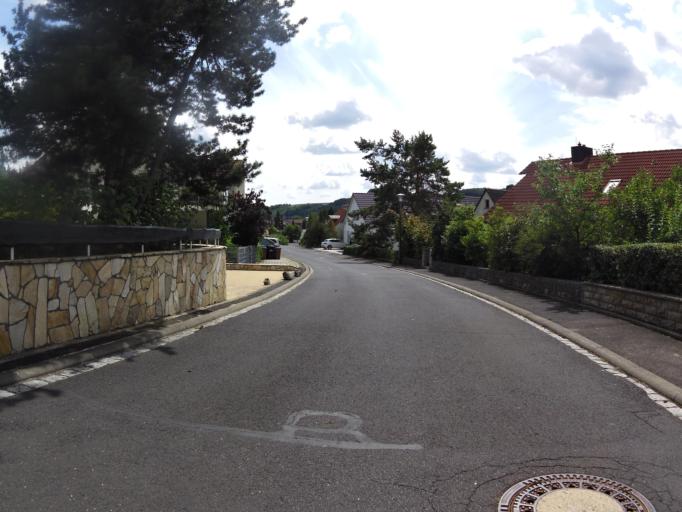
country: DE
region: Bavaria
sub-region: Regierungsbezirk Unterfranken
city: Sommerhausen
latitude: 49.7061
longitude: 10.0270
